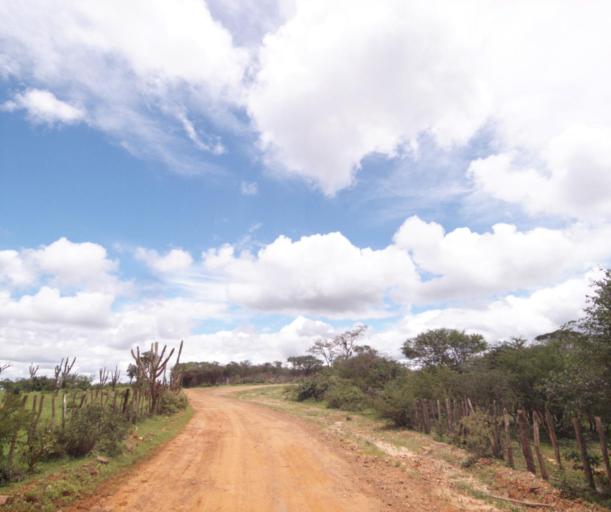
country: BR
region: Bahia
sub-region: Tanhacu
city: Tanhacu
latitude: -14.1897
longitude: -41.0794
